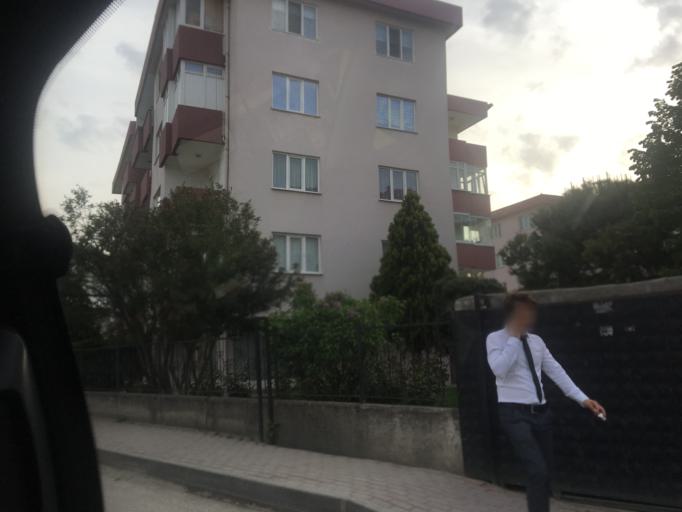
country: TR
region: Bursa
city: Yildirim
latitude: 40.2086
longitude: 29.0297
